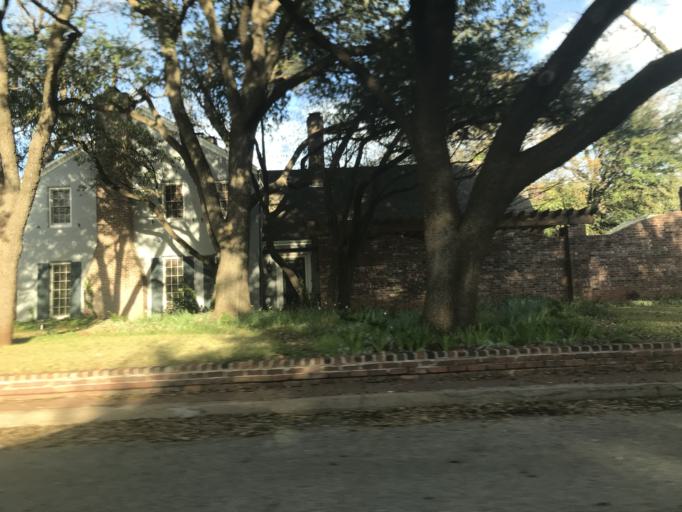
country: US
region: Texas
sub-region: Taylor County
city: Abilene
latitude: 32.4357
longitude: -99.7716
